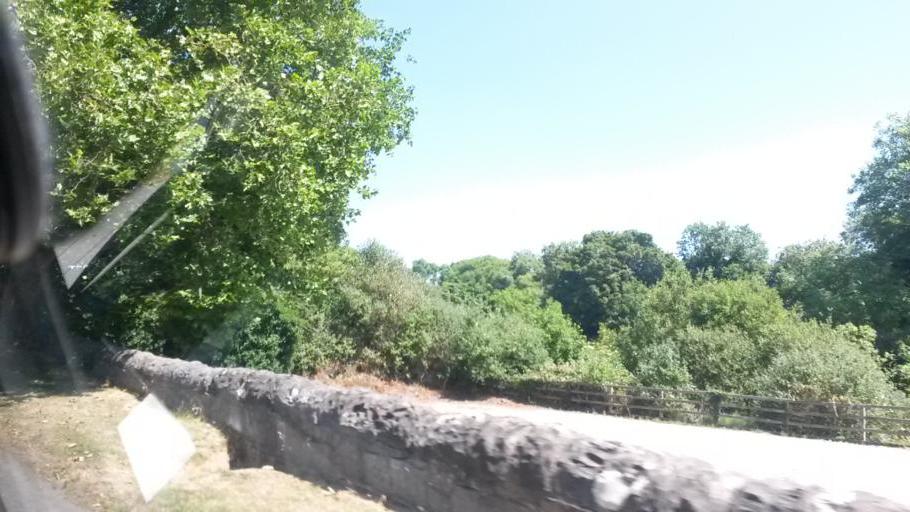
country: IE
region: Leinster
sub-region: An Mhi
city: Ashbourne
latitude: 53.5255
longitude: -6.3145
